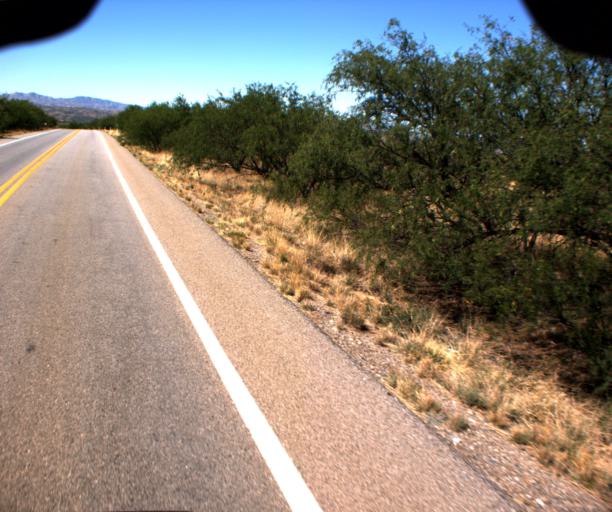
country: US
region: Arizona
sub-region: Santa Cruz County
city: Nogales
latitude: 31.4267
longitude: -110.8444
